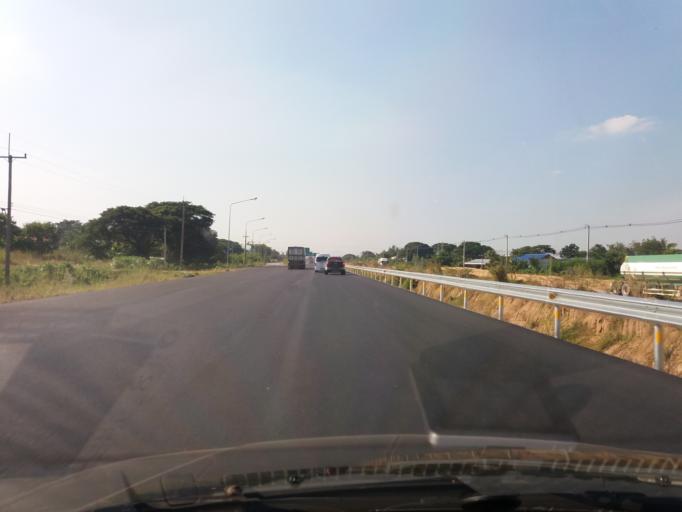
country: TH
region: Nakhon Sawan
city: Krok Phra
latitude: 15.6280
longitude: 100.1072
